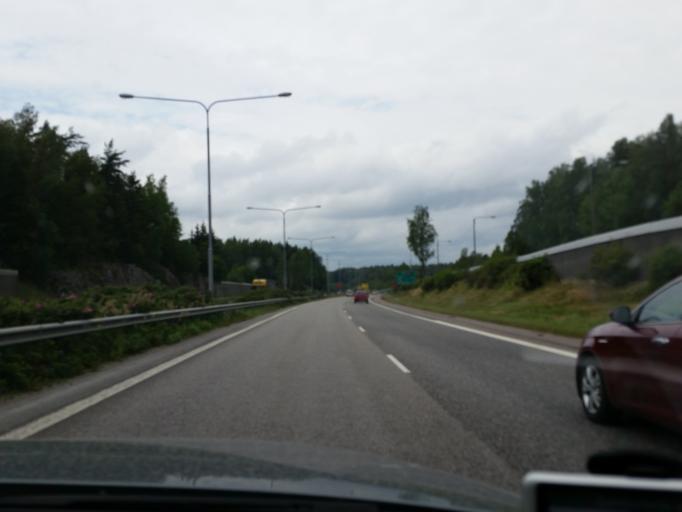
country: FI
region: Uusimaa
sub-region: Helsinki
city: Espoo
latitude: 60.2217
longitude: 24.6330
